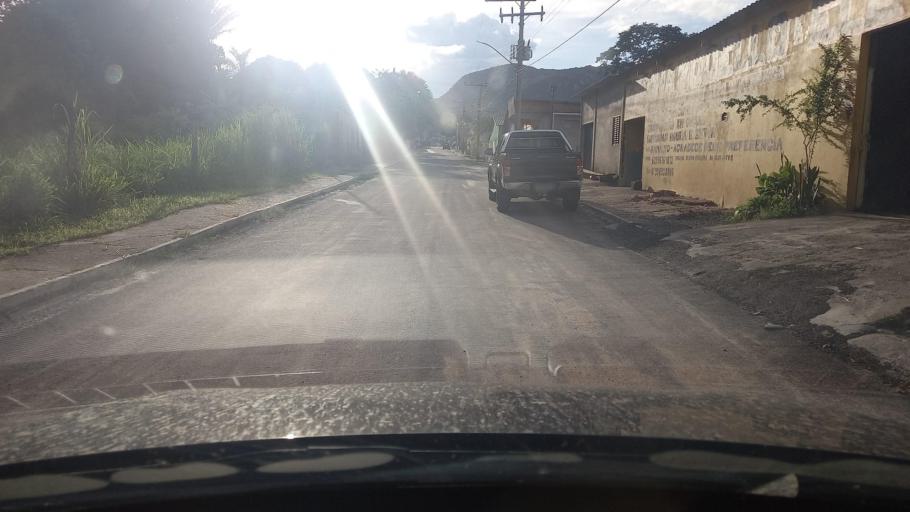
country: BR
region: Goias
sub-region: Cavalcante
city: Cavalcante
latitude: -13.7970
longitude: -47.4568
